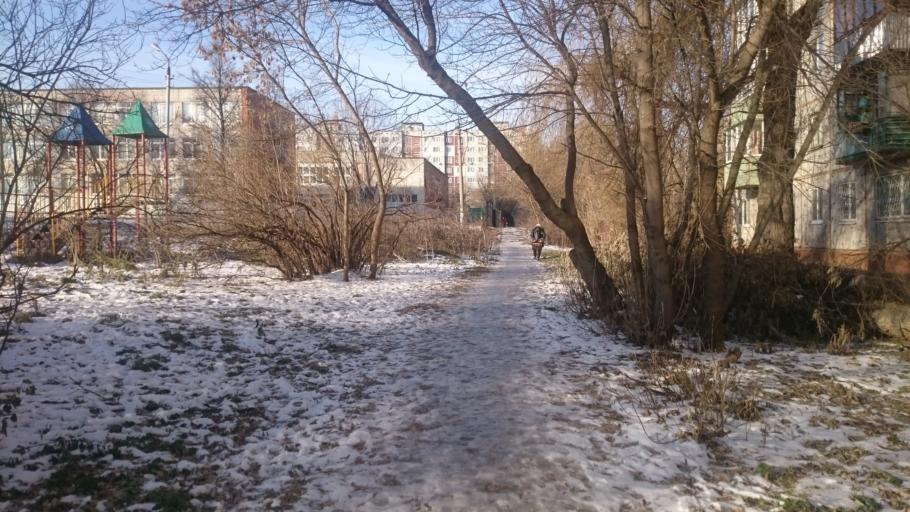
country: RU
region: Tula
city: Tula
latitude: 54.1771
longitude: 37.6379
